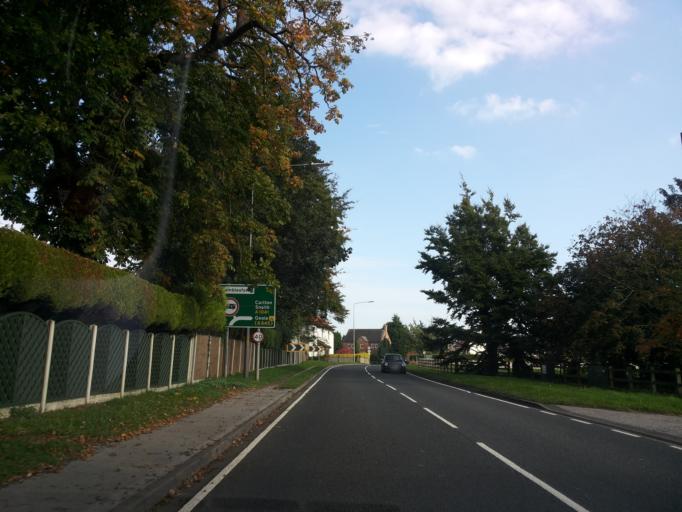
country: GB
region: England
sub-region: North Yorkshire
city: Camblesforth
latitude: 53.7263
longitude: -1.0240
